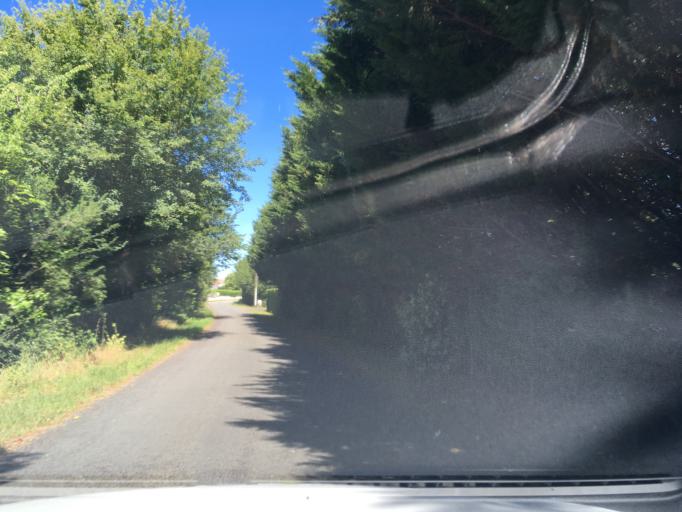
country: FR
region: Poitou-Charentes
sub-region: Departement des Deux-Sevres
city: Aiffres
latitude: 46.3144
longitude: -0.4233
